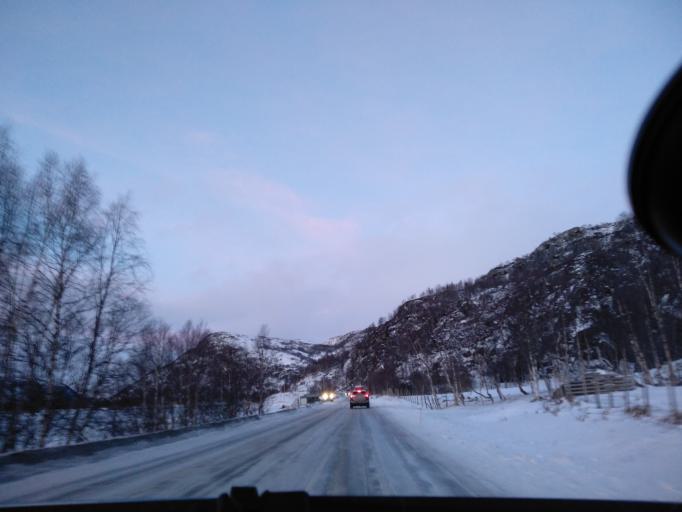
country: NO
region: Vest-Agder
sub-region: Sirdal
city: Tonstad
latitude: 58.9500
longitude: 6.9269
